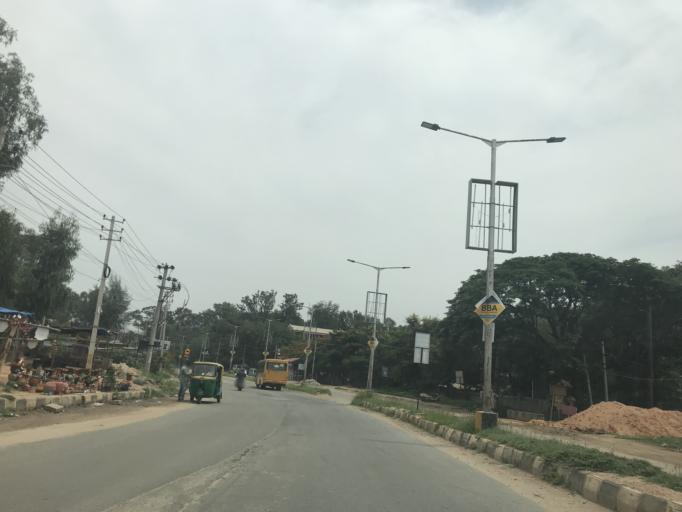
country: IN
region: Karnataka
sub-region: Bangalore Urban
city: Yelahanka
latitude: 13.0758
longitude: 77.6519
